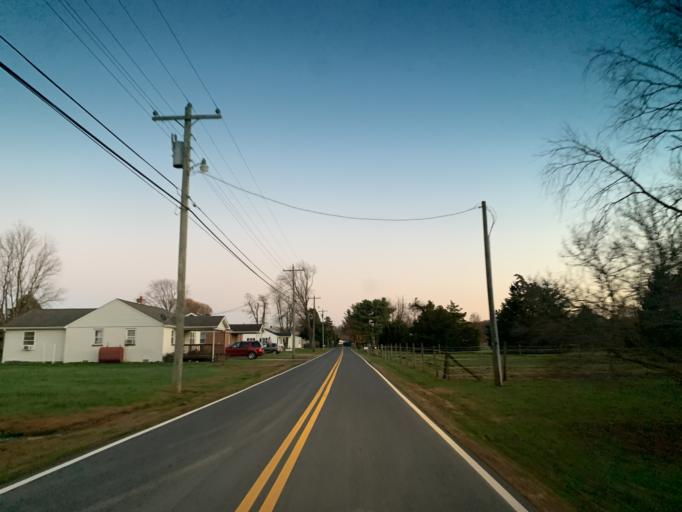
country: US
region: Delaware
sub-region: New Castle County
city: Middletown
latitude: 39.4186
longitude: -75.7804
